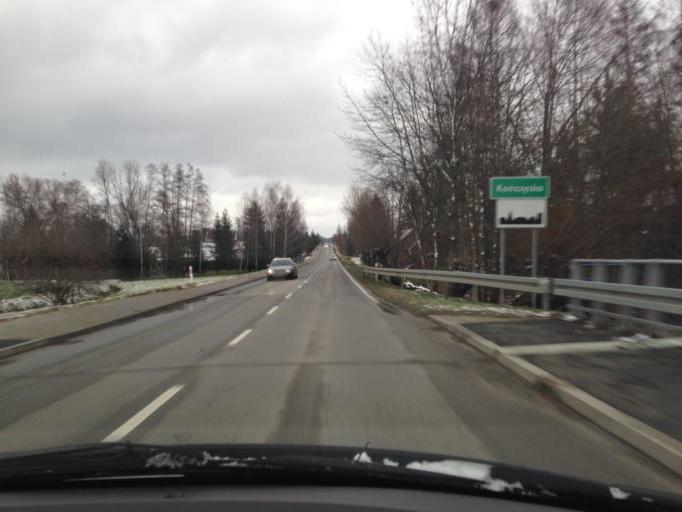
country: PL
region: Lesser Poland Voivodeship
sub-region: Powiat tarnowski
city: Zakliczyn
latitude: 49.8546
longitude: 20.8204
